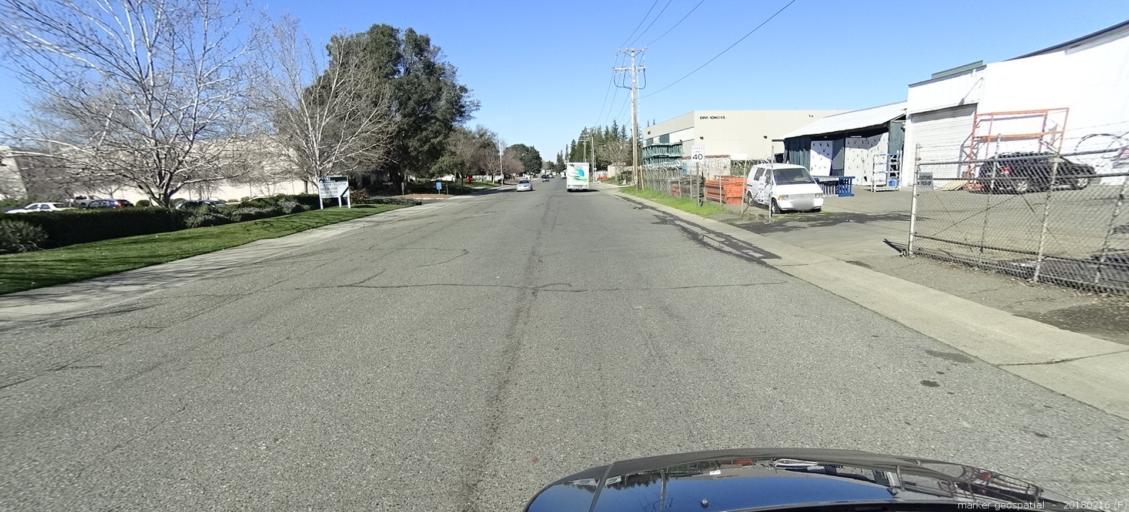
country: US
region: California
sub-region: Sacramento County
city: Gold River
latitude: 38.6145
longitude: -121.2597
